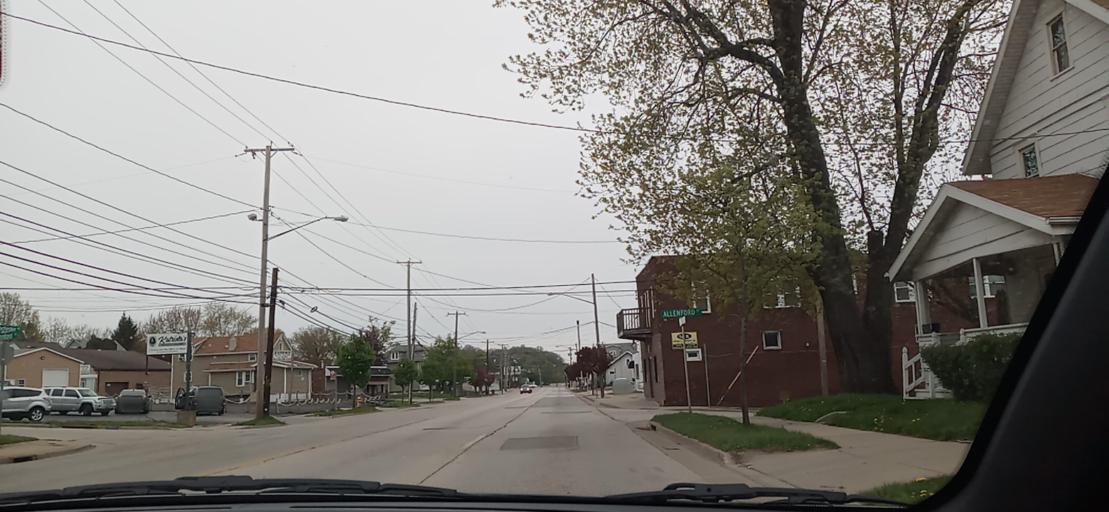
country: US
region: Ohio
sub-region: Summit County
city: Portage Lakes
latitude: 41.0363
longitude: -81.5455
